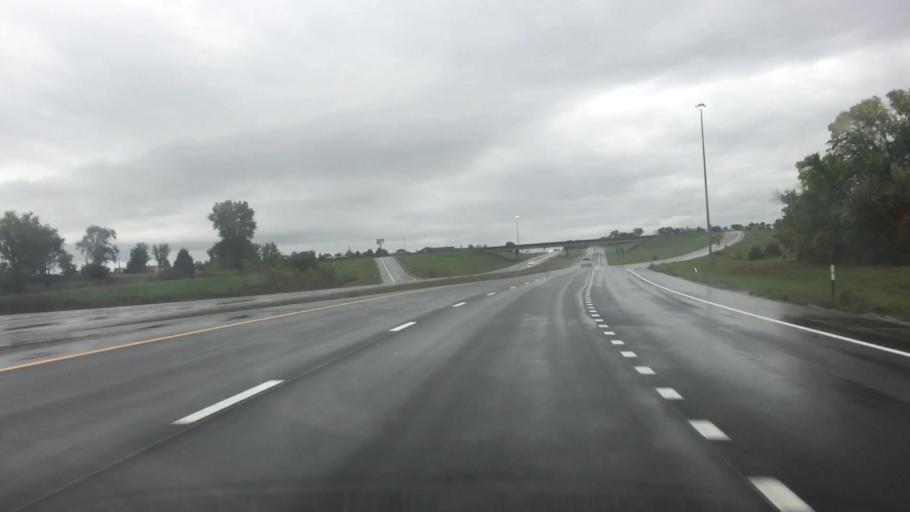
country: US
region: Kansas
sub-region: Johnson County
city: Spring Hill
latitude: 38.7280
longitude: -94.8338
